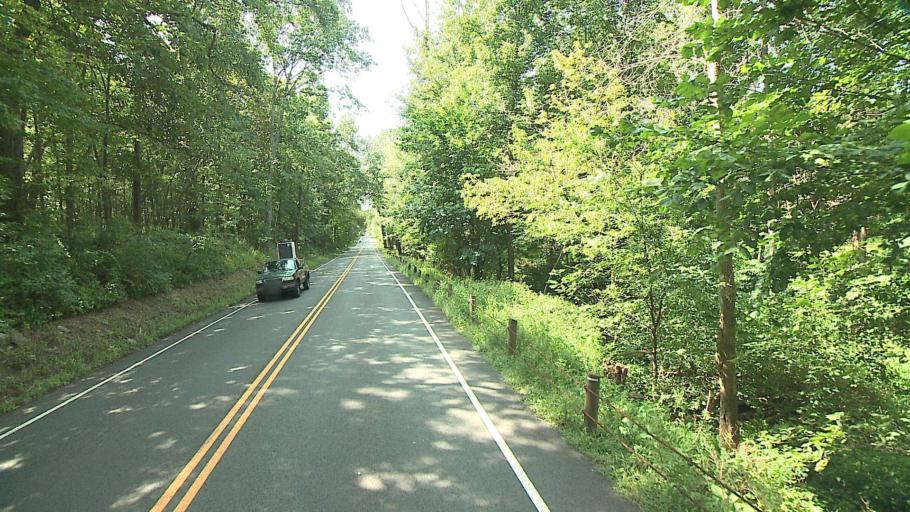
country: US
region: Connecticut
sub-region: Fairfield County
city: Trumbull
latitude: 41.2968
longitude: -73.2874
